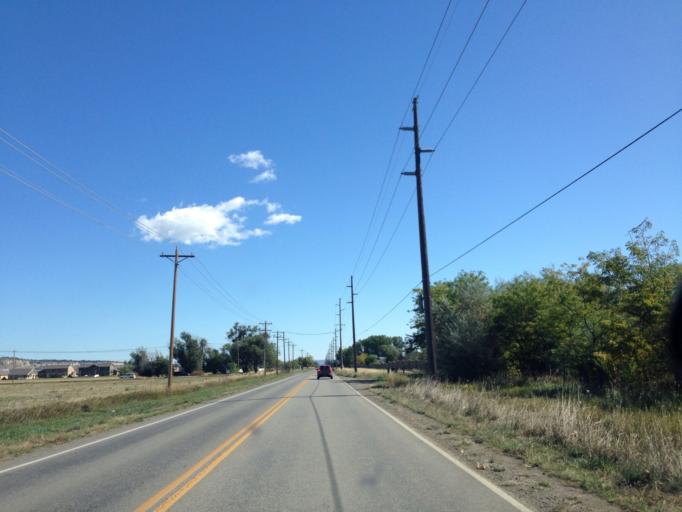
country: US
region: Montana
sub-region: Yellowstone County
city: Billings
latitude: 45.7841
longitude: -108.6553
